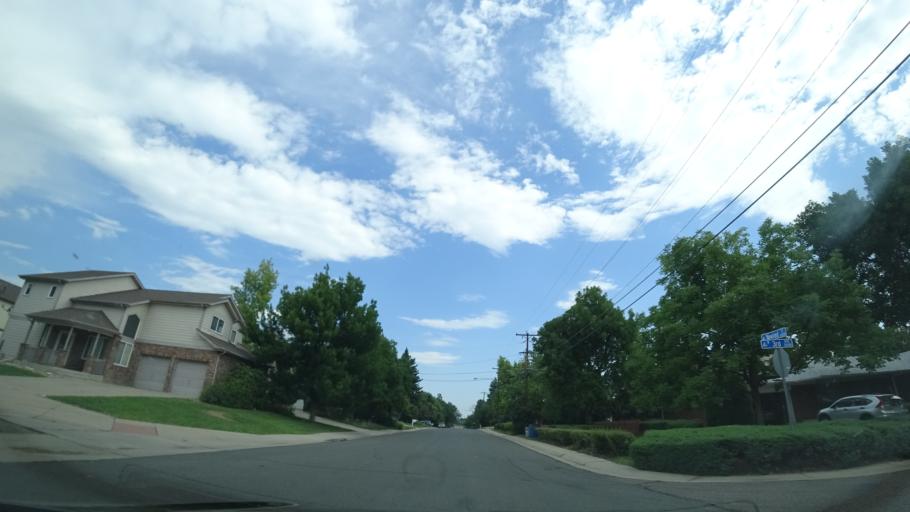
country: US
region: Colorado
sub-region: Jefferson County
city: Lakewood
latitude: 39.7217
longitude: -105.0699
